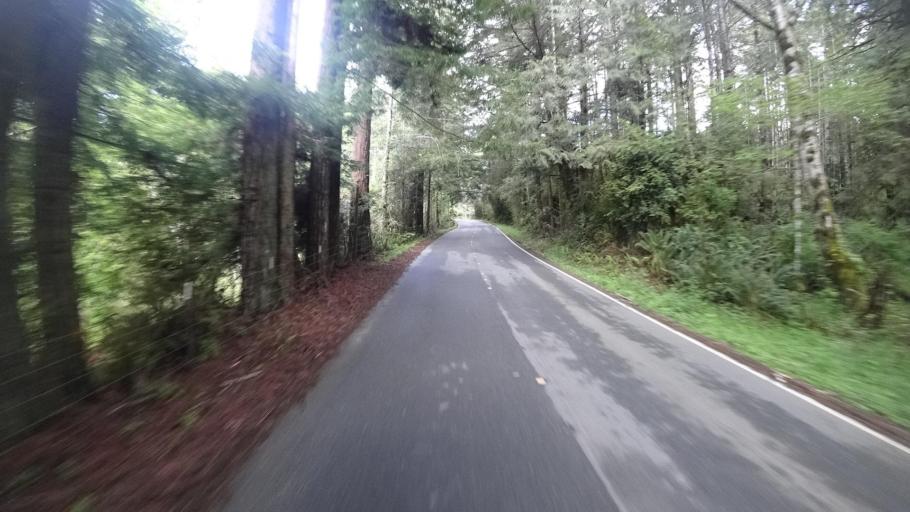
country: US
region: California
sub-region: Humboldt County
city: Blue Lake
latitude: 40.9319
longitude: -124.0190
